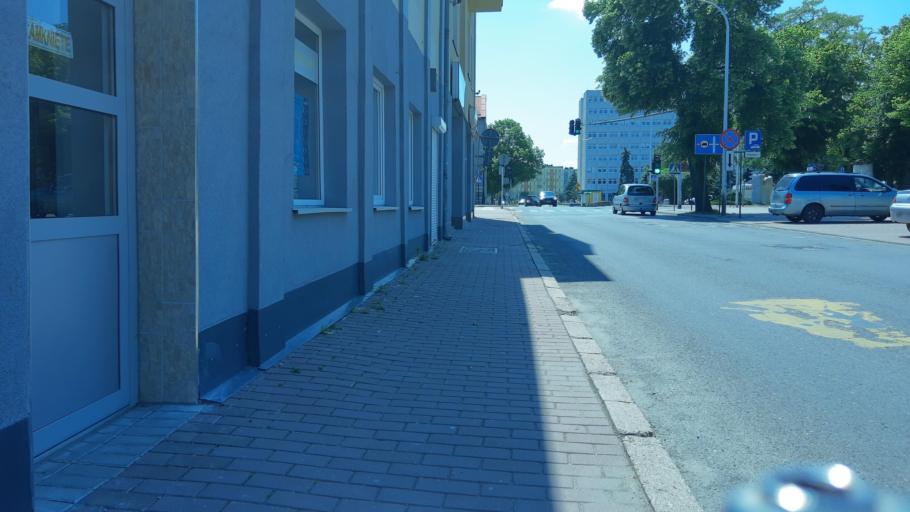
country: PL
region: Lodz Voivodeship
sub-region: Powiat sieradzki
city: Sieradz
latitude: 51.5950
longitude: 18.7350
